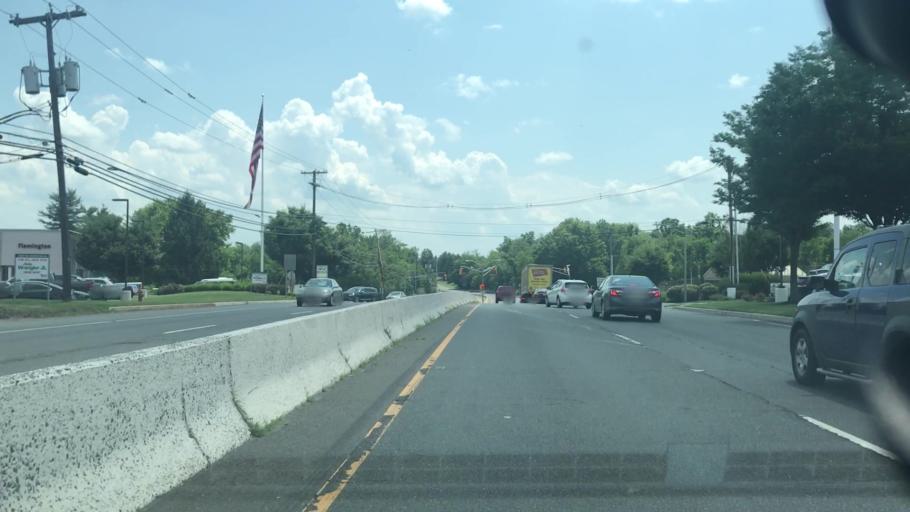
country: US
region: New Jersey
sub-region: Hunterdon County
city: Flemington
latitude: 40.4862
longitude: -74.8633
